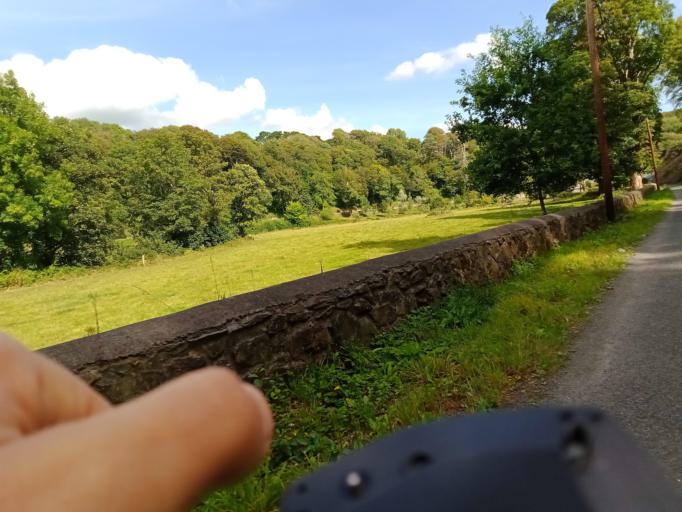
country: IE
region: Munster
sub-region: Waterford
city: Dungarvan
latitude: 52.1243
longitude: -7.4647
